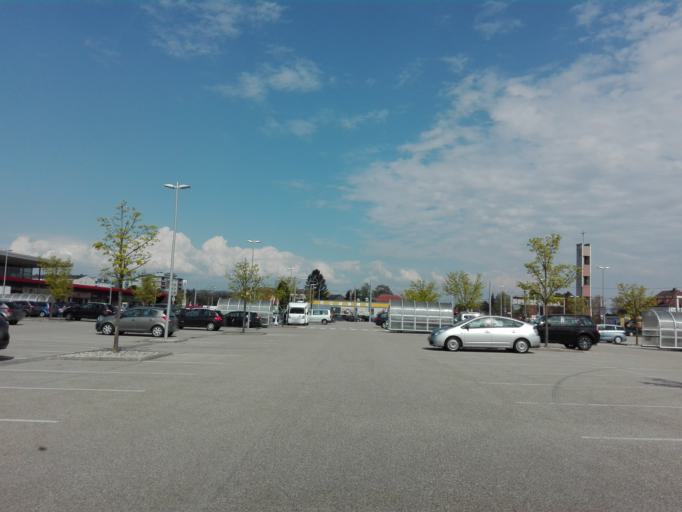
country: AT
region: Upper Austria
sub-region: Politischer Bezirk Linz-Land
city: Leonding
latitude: 48.2551
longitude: 14.2854
